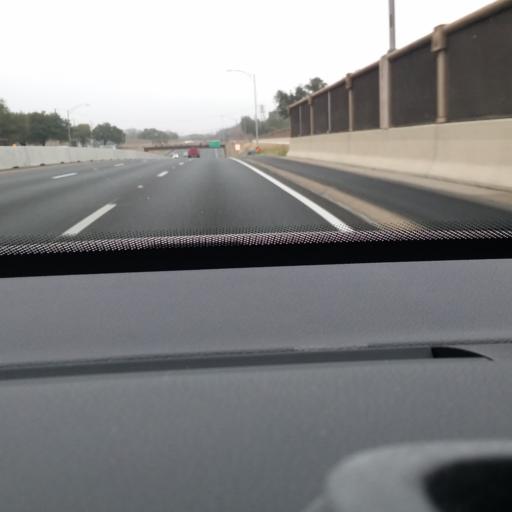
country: US
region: Texas
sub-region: Dallas County
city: Highland Park
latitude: 32.8444
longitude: -96.7861
